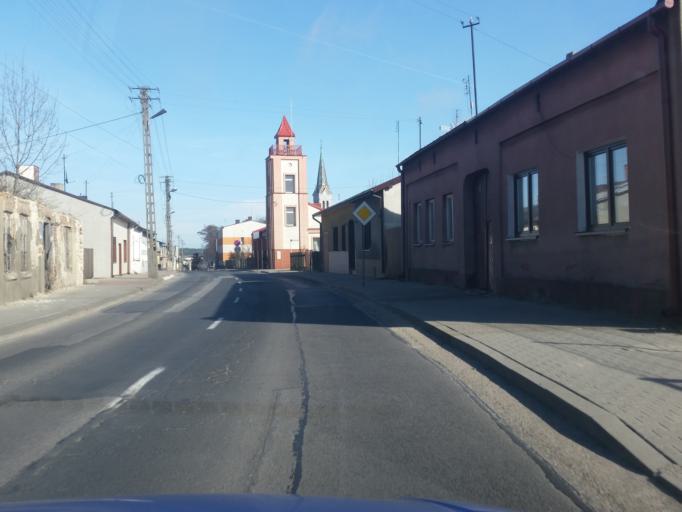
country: PL
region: Lodz Voivodeship
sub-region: Powiat radomszczanski
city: Kamiensk
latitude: 51.2054
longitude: 19.4952
